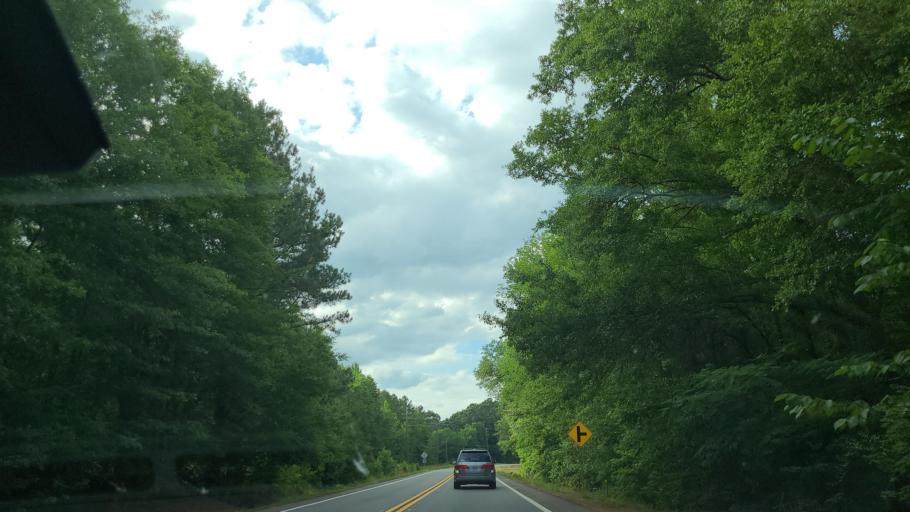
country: US
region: Georgia
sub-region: Putnam County
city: Eatonton
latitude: 33.2223
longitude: -83.4299
